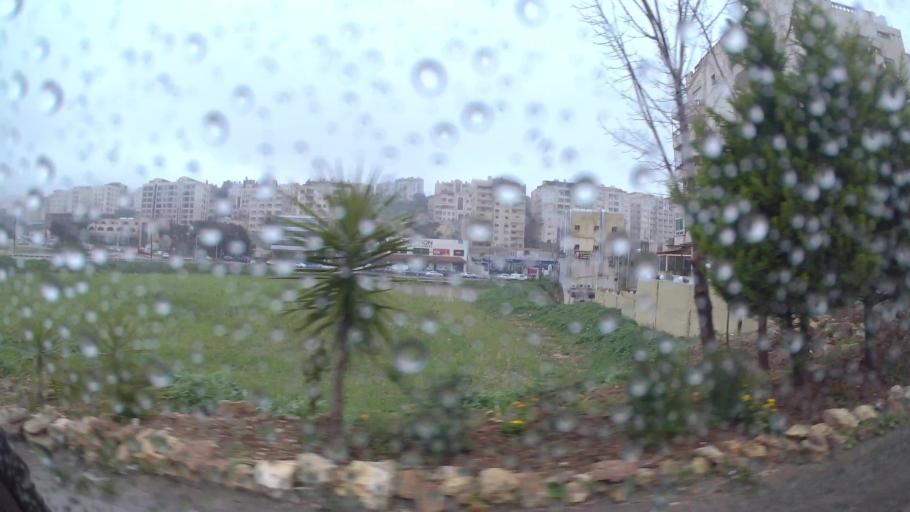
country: JO
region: Amman
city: Al Jubayhah
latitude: 32.0054
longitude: 35.8313
